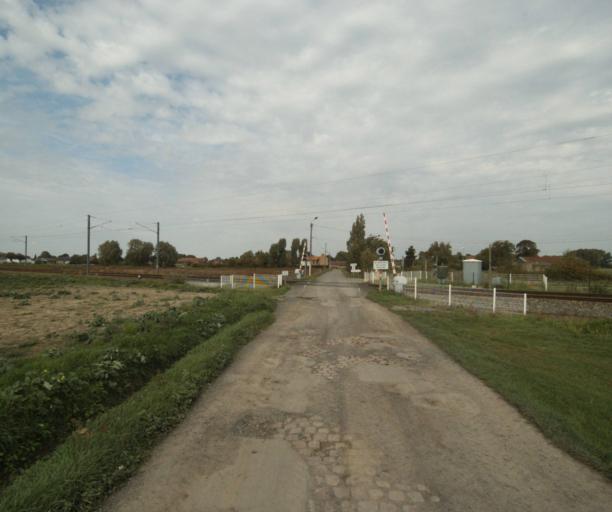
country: FR
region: Nord-Pas-de-Calais
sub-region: Departement du Nord
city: Marquillies
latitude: 50.5477
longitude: 2.8767
